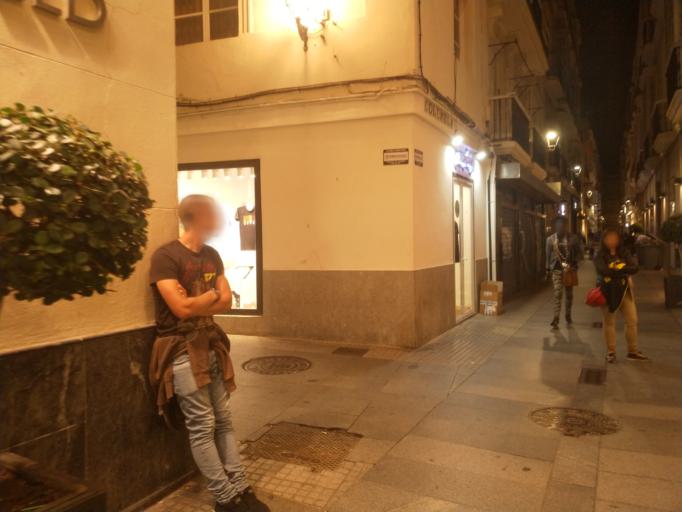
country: ES
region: Andalusia
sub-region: Provincia de Cadiz
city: Cadiz
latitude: 36.5324
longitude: -6.2959
